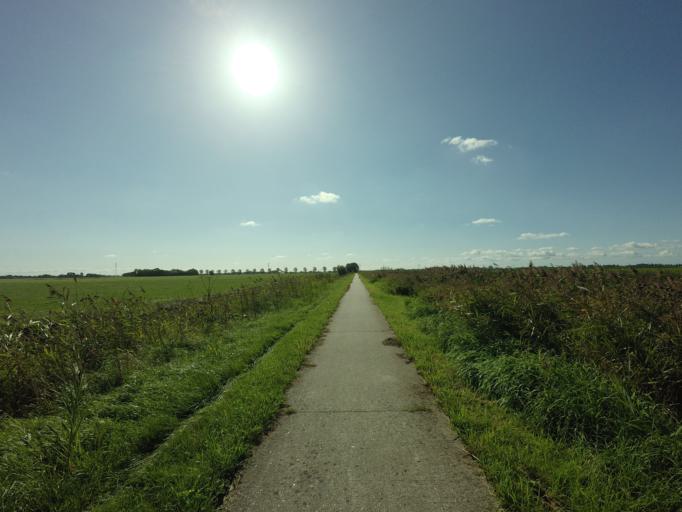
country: NL
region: Friesland
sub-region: Gemeente Boarnsterhim
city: Reduzum
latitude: 53.1243
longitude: 5.7549
